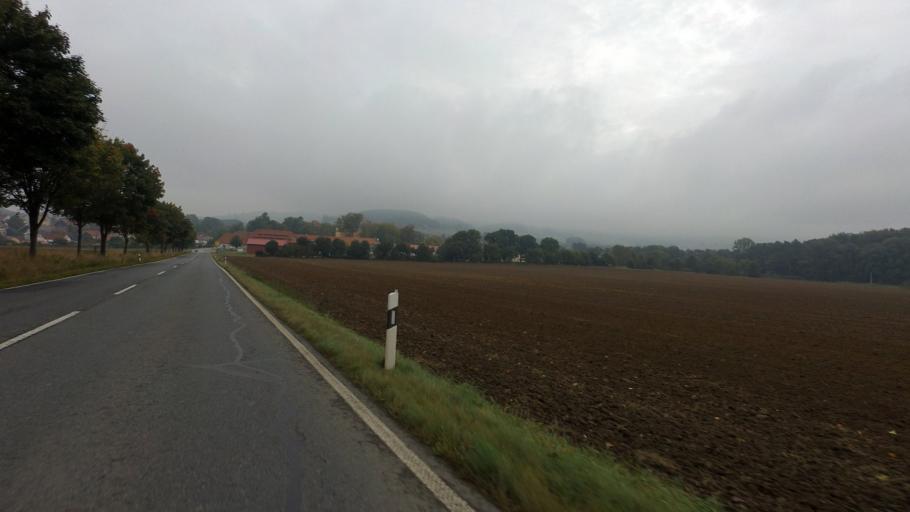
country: DE
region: Saxony
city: Neustadt in Sachsen
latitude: 51.0196
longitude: 14.2324
